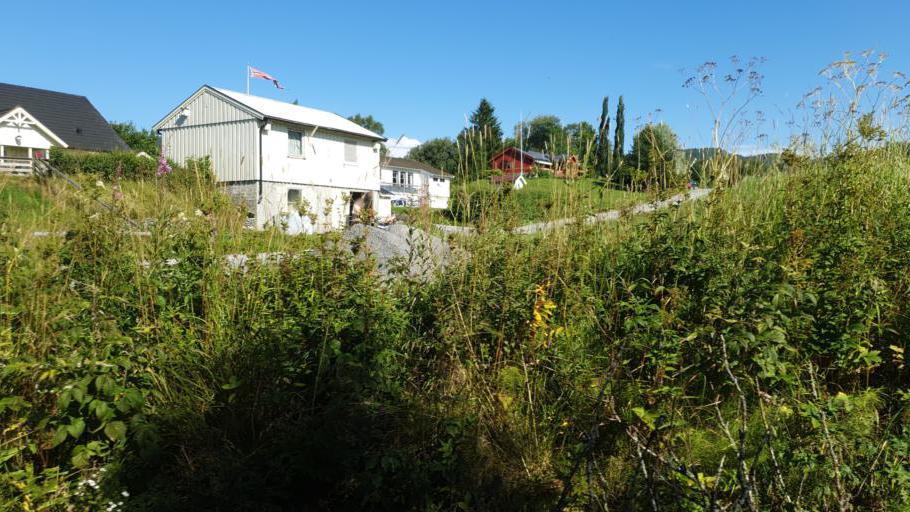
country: NO
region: Sor-Trondelag
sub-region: Orkdal
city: Orkanger
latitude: 63.2013
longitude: 9.7822
